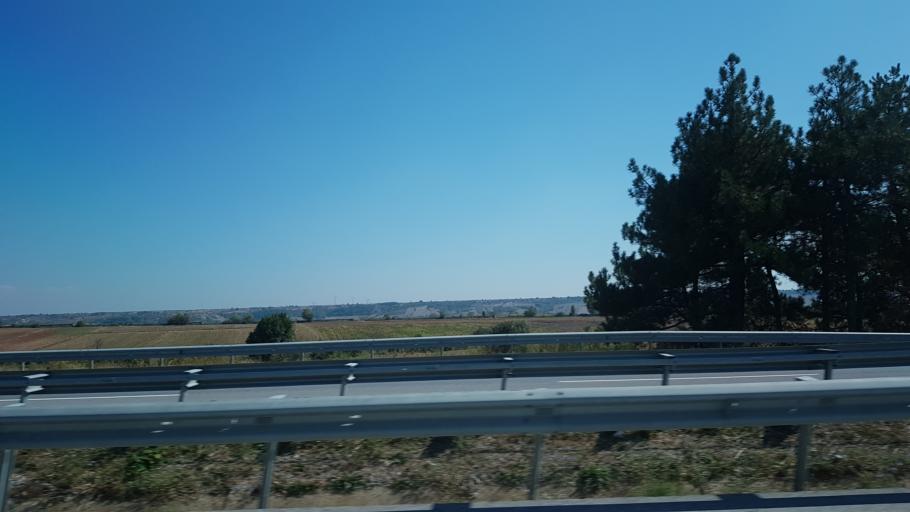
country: TR
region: Kirklareli
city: Babaeski
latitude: 41.5347
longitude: 27.1266
